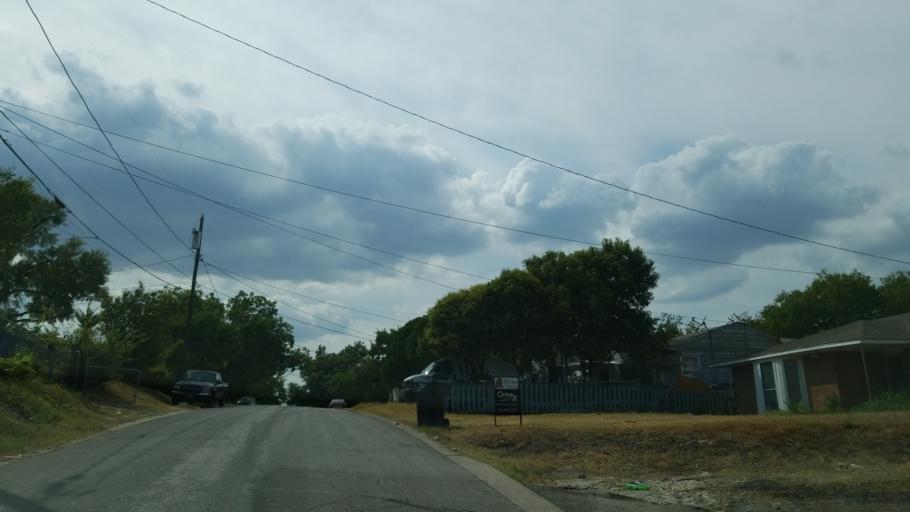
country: US
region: Texas
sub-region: Dallas County
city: Dallas
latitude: 32.7696
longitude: -96.8465
